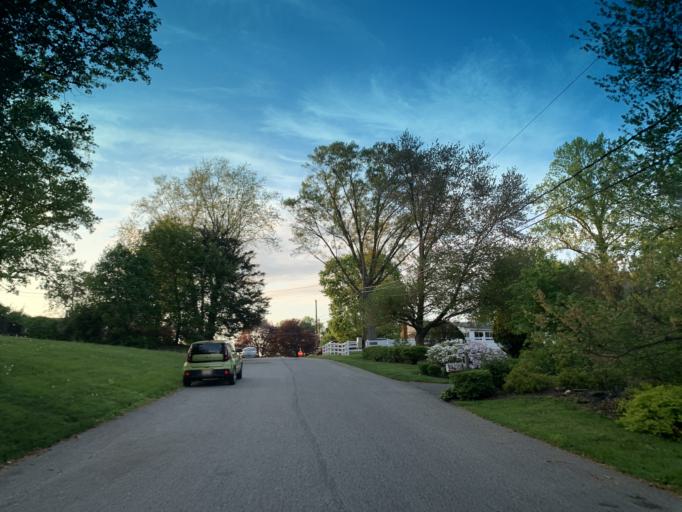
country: US
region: Maryland
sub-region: Harford County
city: Bel Air South
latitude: 39.4983
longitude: -76.3380
